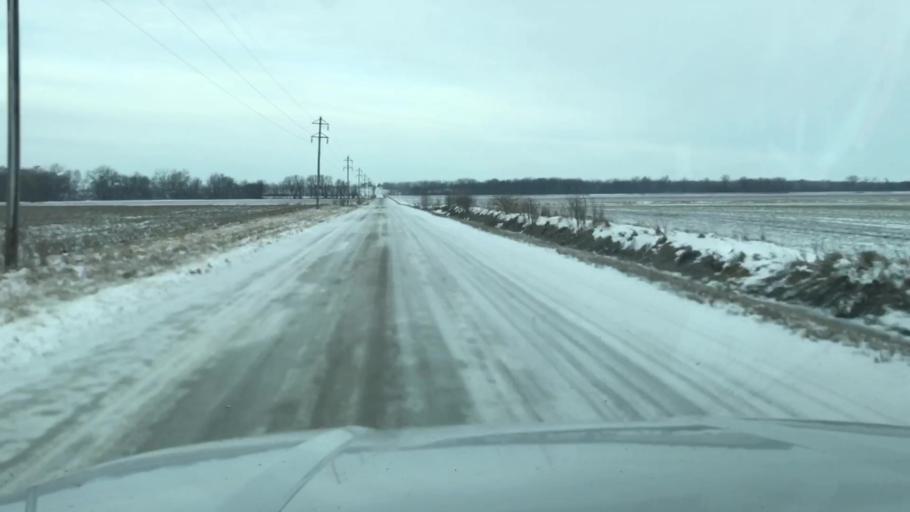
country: US
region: Missouri
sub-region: Holt County
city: Oregon
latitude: 40.1300
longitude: -95.0342
